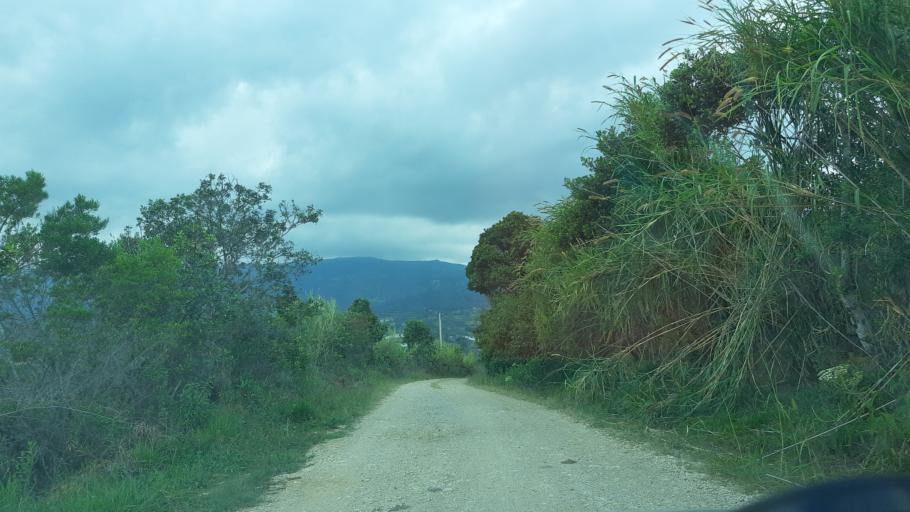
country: CO
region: Boyaca
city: Santa Sofia
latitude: 5.7466
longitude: -73.5720
